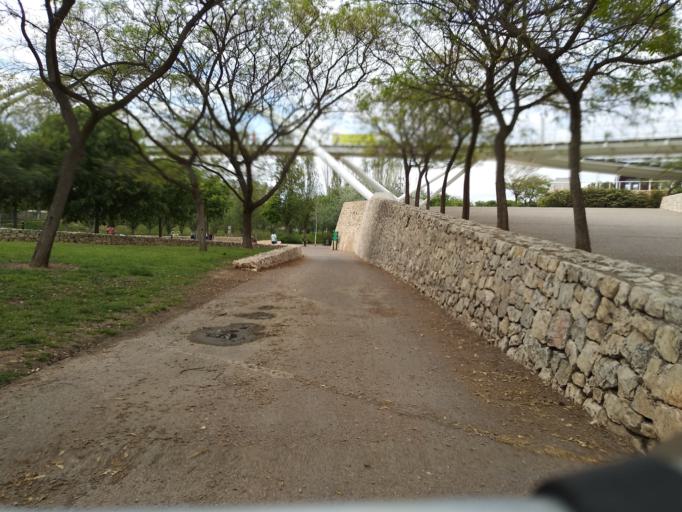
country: ES
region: Valencia
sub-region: Provincia de Valencia
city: Mislata
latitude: 39.4775
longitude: -0.4081
